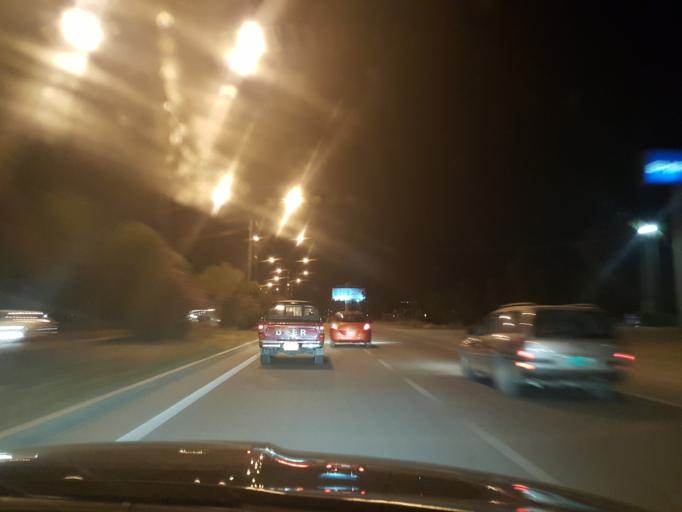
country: IQ
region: Arbil
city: Erbil
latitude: 36.2634
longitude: 44.0906
